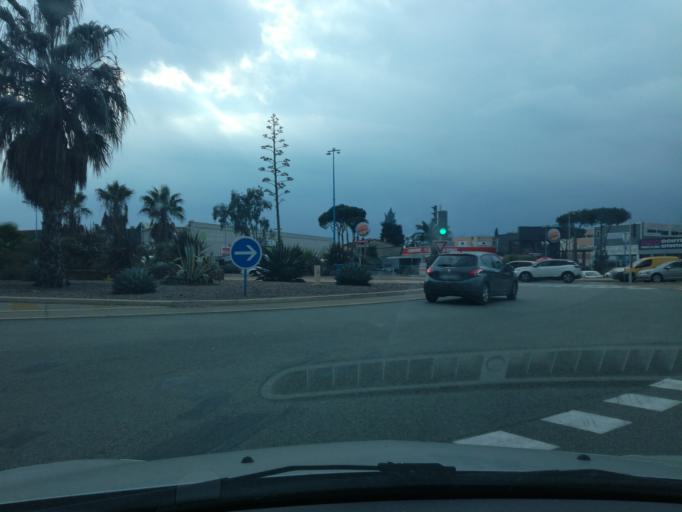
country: FR
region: Provence-Alpes-Cote d'Azur
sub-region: Departement des Alpes-Maritimes
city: Mandelieu-la-Napoule
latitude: 43.5570
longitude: 6.9530
